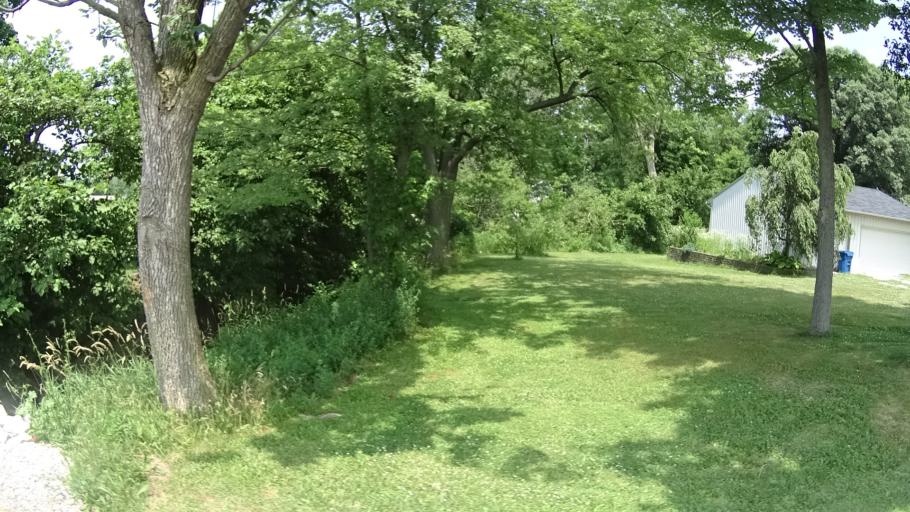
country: US
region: Ohio
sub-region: Lorain County
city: Vermilion
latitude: 41.4102
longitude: -82.3710
